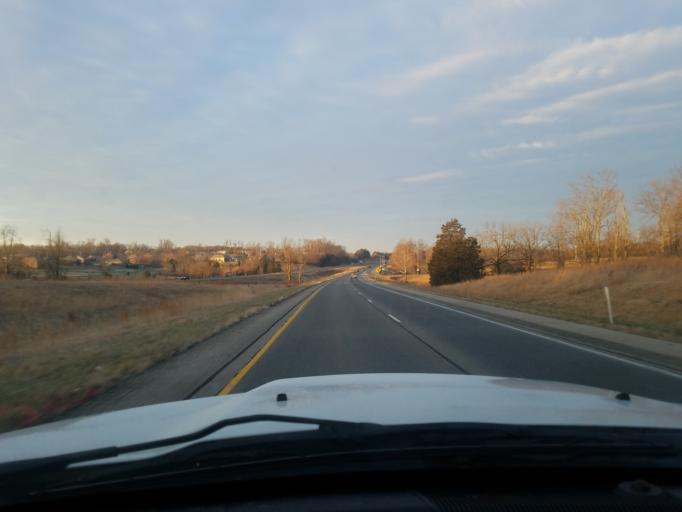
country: US
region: Indiana
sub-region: Floyd County
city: Georgetown
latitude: 38.2736
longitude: -85.9655
